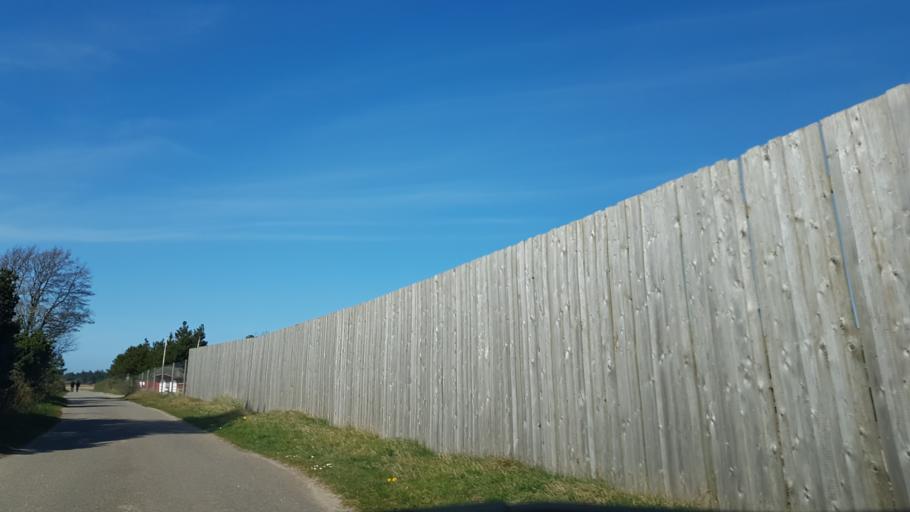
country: DE
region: Schleswig-Holstein
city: List
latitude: 55.0969
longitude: 8.5490
